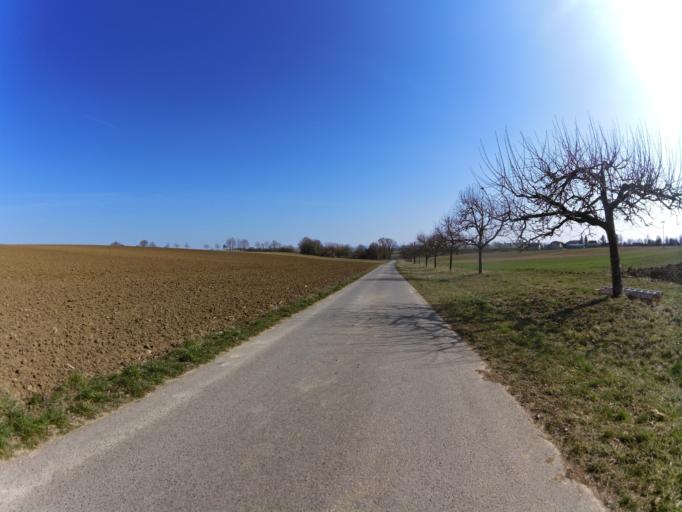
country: DE
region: Bavaria
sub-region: Regierungsbezirk Unterfranken
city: Prosselsheim
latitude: 49.8260
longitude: 10.1086
